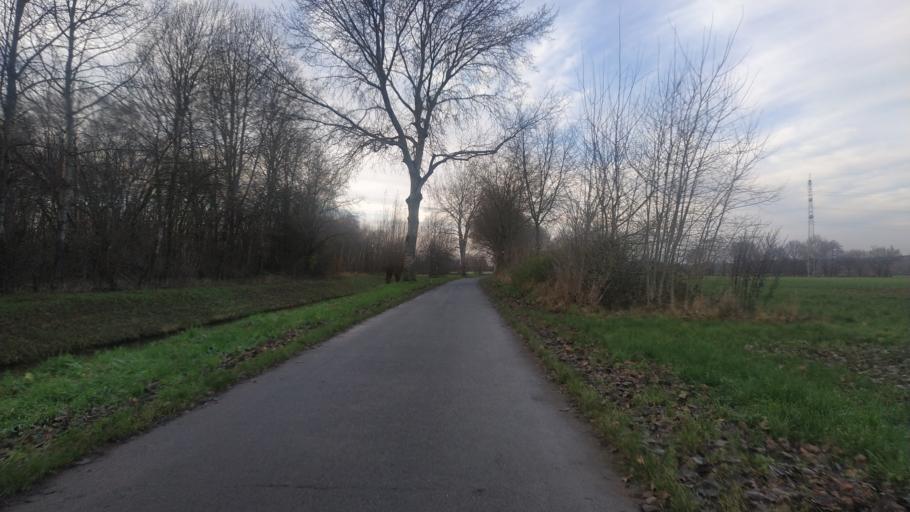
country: DE
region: North Rhine-Westphalia
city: Ibbenburen
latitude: 52.2801
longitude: 7.6838
